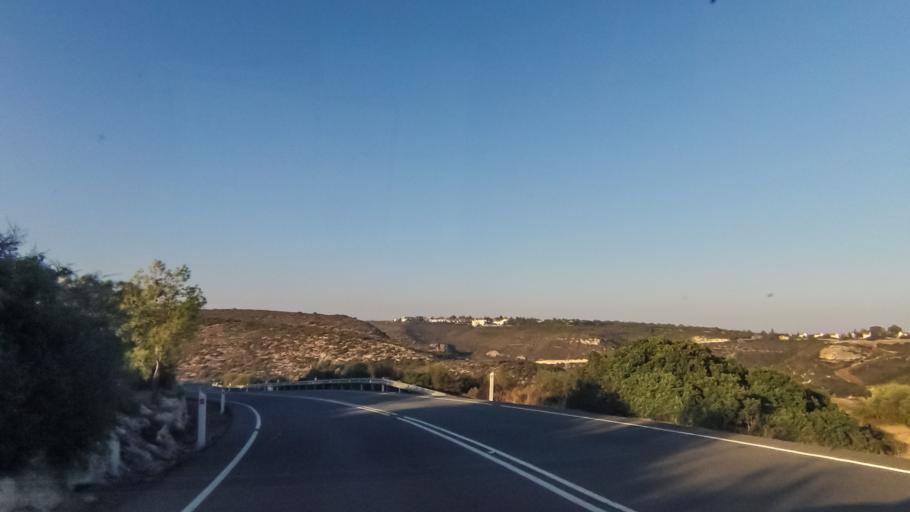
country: CY
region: Limassol
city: Sotira
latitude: 34.6720
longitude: 32.8139
